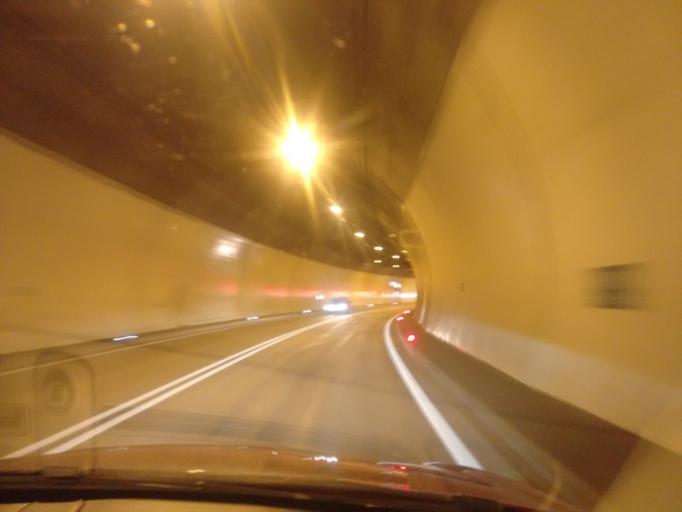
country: AT
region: Upper Austria
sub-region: Politischer Bezirk Gmunden
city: Ebensee
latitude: 47.8495
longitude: 13.7781
